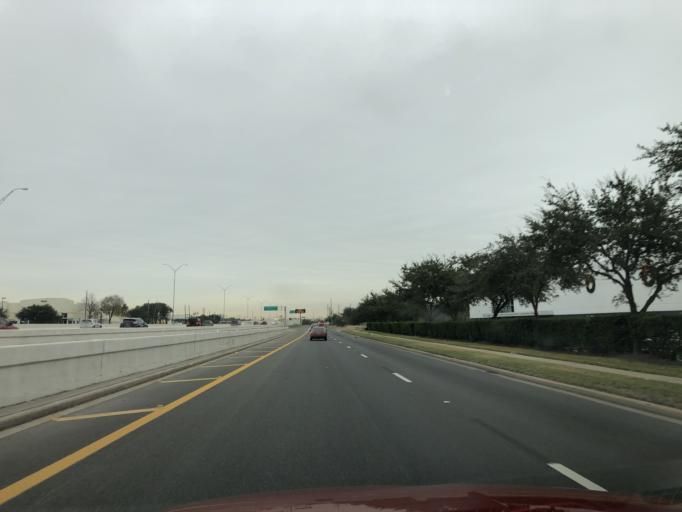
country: US
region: Texas
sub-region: Fort Bend County
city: Missouri City
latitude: 29.6399
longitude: -95.5336
